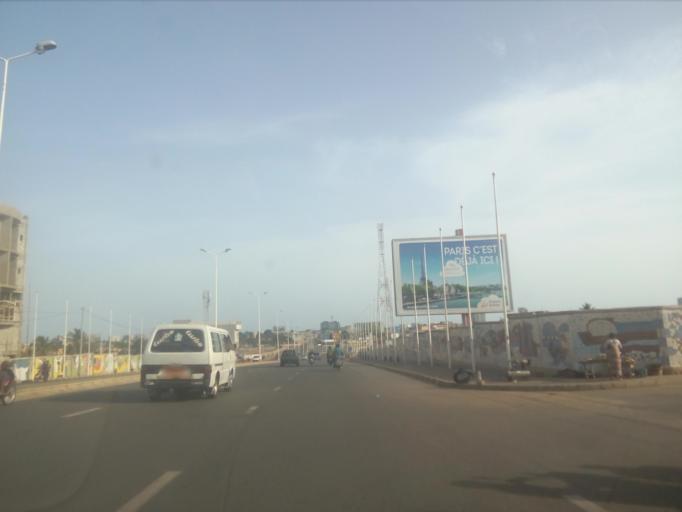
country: TG
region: Maritime
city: Lome
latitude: 6.1490
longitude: 1.2295
